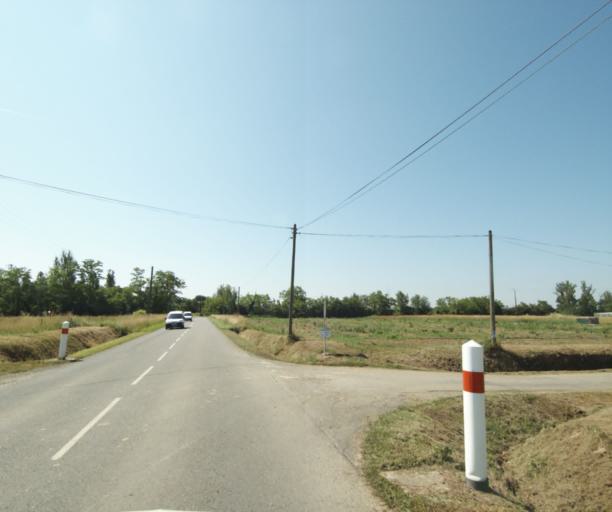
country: FR
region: Midi-Pyrenees
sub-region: Departement du Tarn-et-Garonne
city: Montbeton
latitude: 44.0442
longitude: 1.2933
